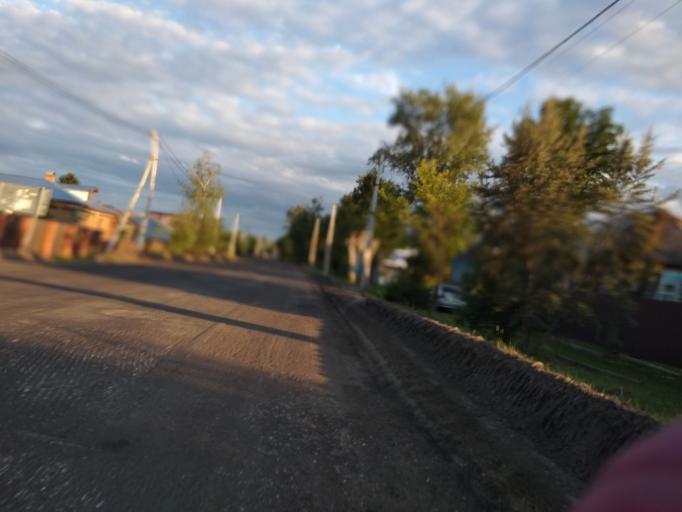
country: RU
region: Moskovskaya
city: Misheronskiy
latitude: 55.6562
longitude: 39.7520
